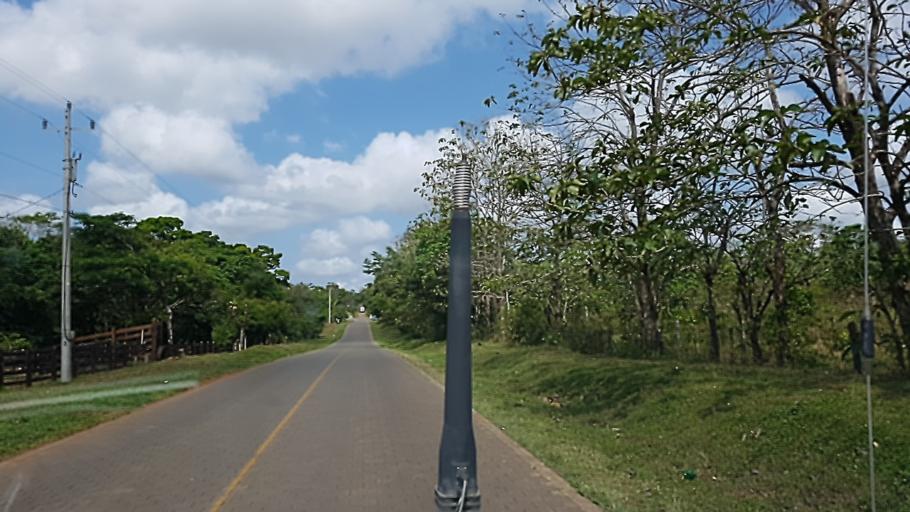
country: NI
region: Atlantico Sur
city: Nueva Guinea
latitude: 11.6797
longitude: -84.4463
